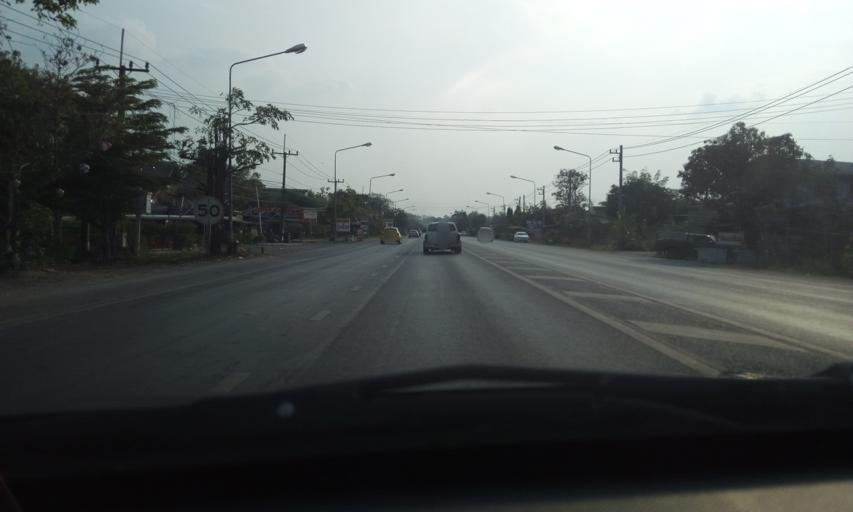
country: TH
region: Nakhon Nayok
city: Nakhon Nayok
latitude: 14.2152
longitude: 101.2256
